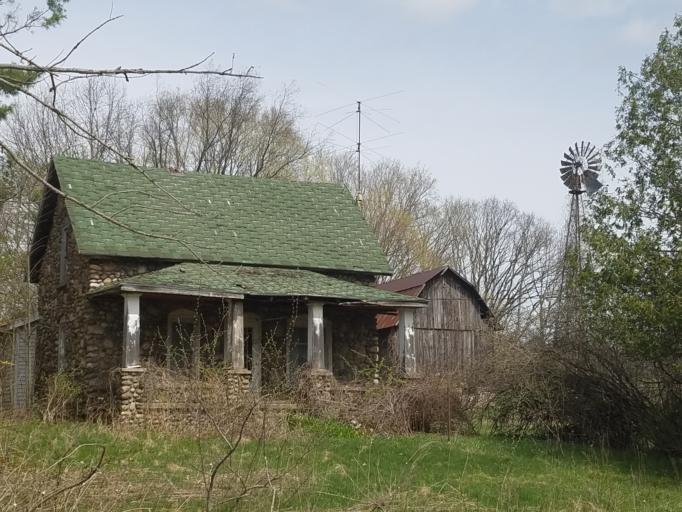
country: US
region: Michigan
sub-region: Isabella County
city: Lake Isabella
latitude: 43.5819
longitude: -84.9643
